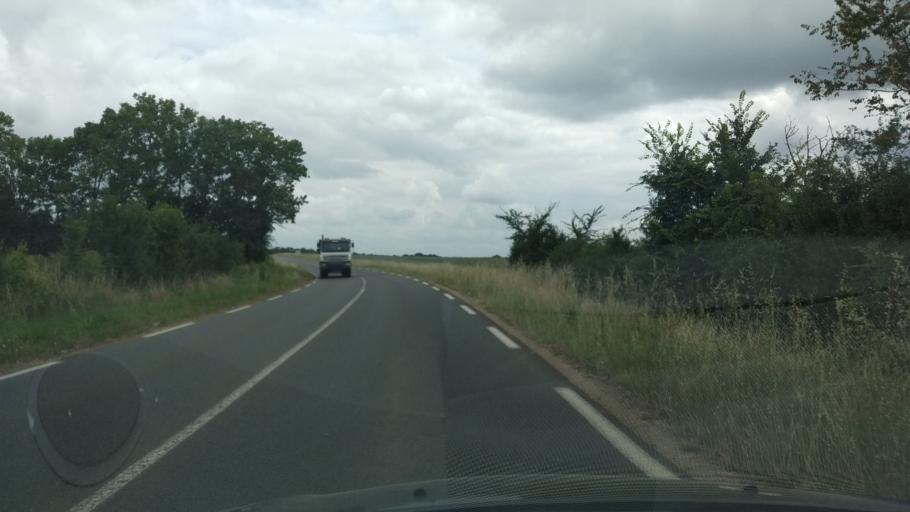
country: FR
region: Poitou-Charentes
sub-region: Departement de la Vienne
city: La Villedieu-du-Clain
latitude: 46.4395
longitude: 0.3710
